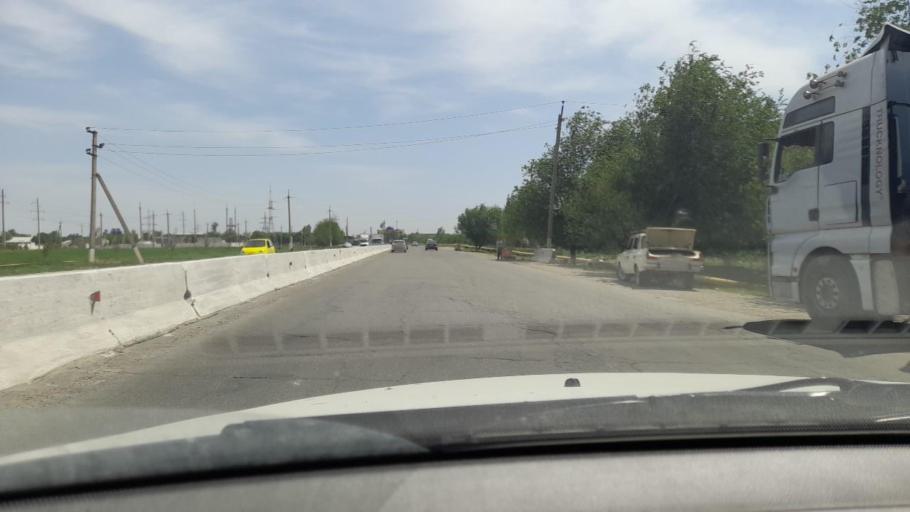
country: UZ
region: Bukhara
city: Ghijduwon
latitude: 40.0856
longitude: 64.6782
